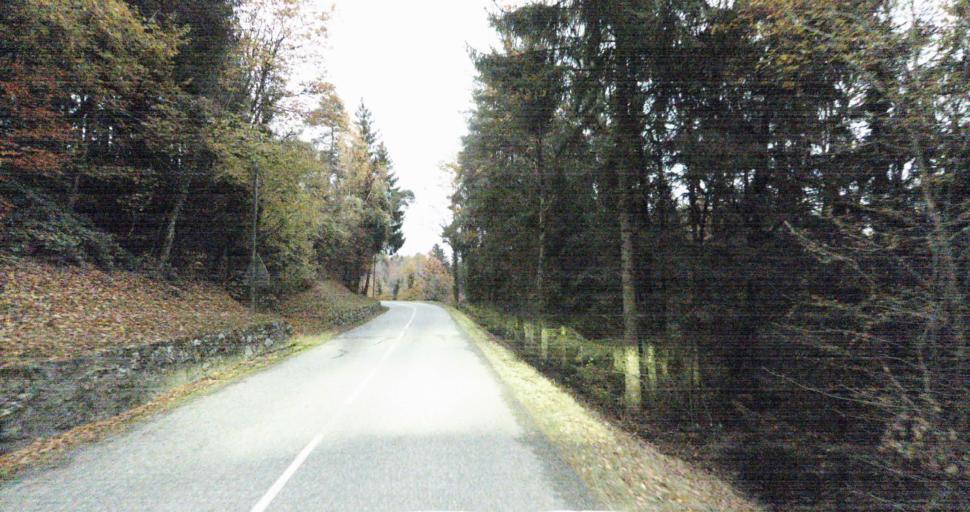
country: FR
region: Rhone-Alpes
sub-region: Departement de la Haute-Savoie
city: Saint-Jorioz
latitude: 45.8304
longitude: 6.1411
